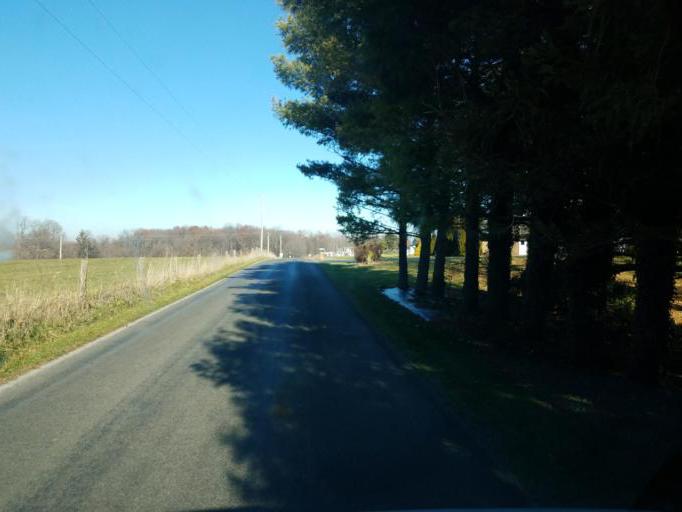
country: US
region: Ohio
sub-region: Wayne County
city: Apple Creek
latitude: 40.6946
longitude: -81.8034
